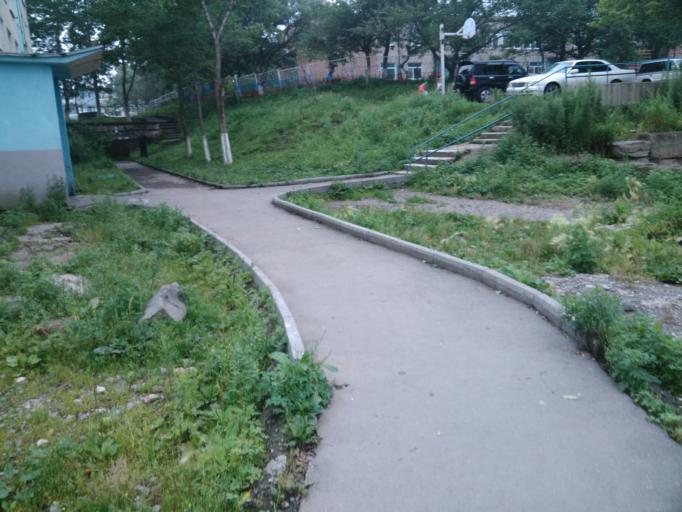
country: RU
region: Primorskiy
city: Vladivostok
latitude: 43.0958
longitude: 131.9758
